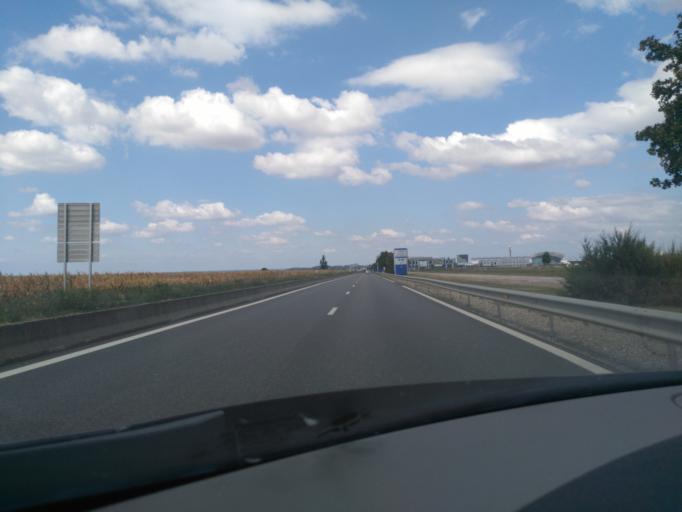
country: FR
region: Rhone-Alpes
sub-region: Departement du Rhone
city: Saint-Laurent-de-Mure
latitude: 45.7069
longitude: 5.0717
